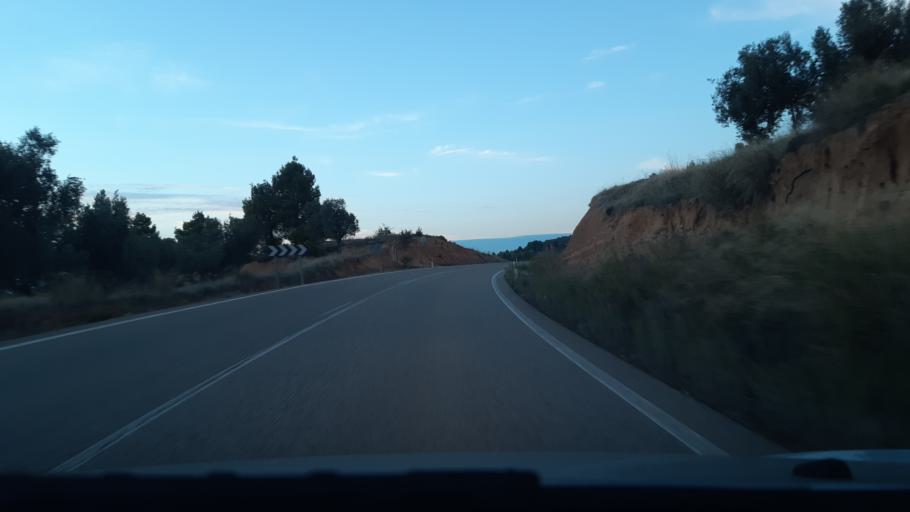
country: ES
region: Aragon
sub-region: Provincia de Teruel
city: Valderrobres
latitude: 40.8590
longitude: 0.1693
